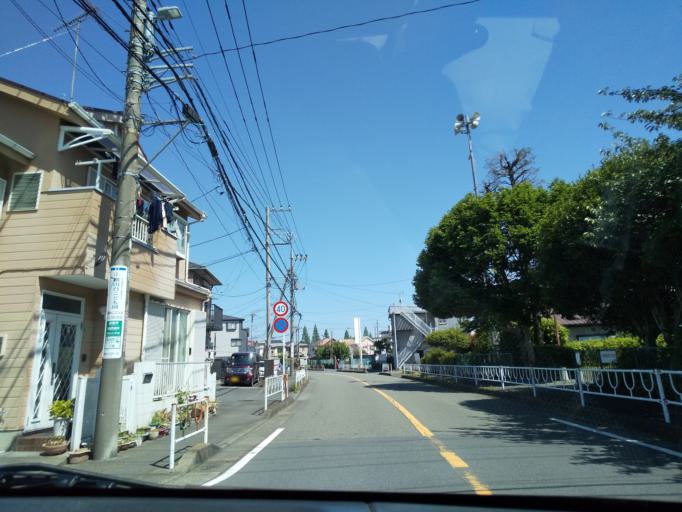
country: JP
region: Kanagawa
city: Zama
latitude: 35.5648
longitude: 139.3572
